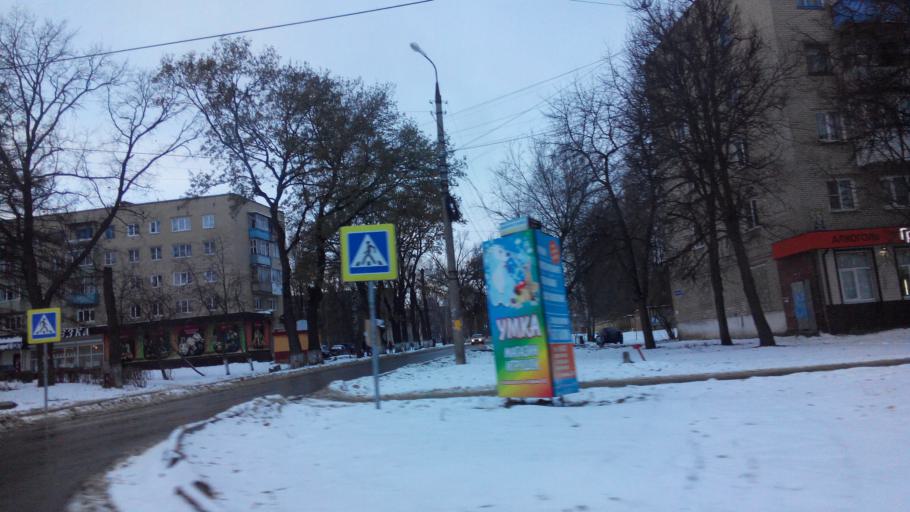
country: RU
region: Tula
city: Uzlovaya
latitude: 53.9760
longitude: 38.1885
